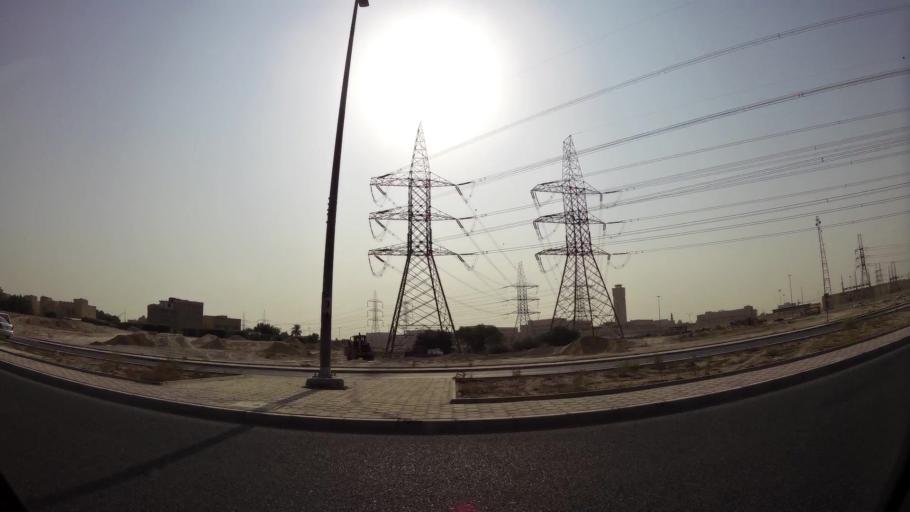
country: KW
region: Al Asimah
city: Ar Rabiyah
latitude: 29.2968
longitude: 47.8541
